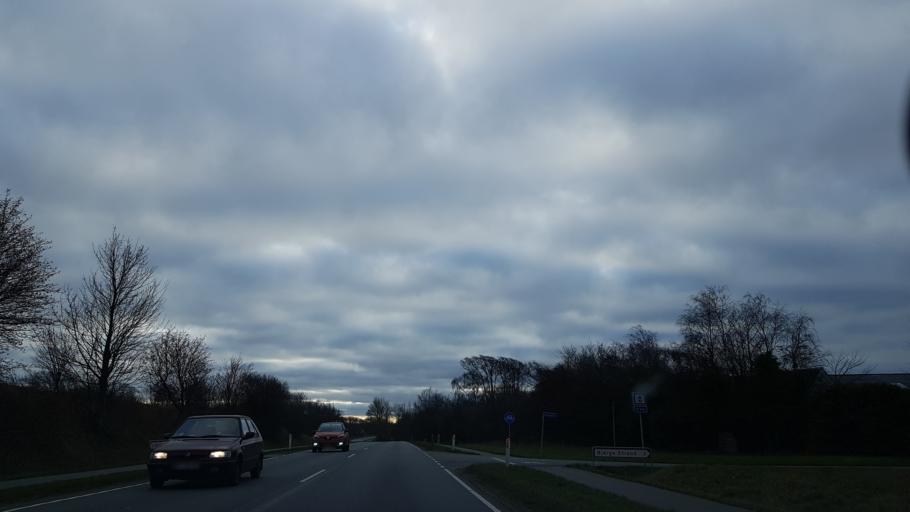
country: DK
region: Zealand
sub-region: Kalundborg Kommune
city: Gorlev
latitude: 55.5699
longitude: 11.1949
